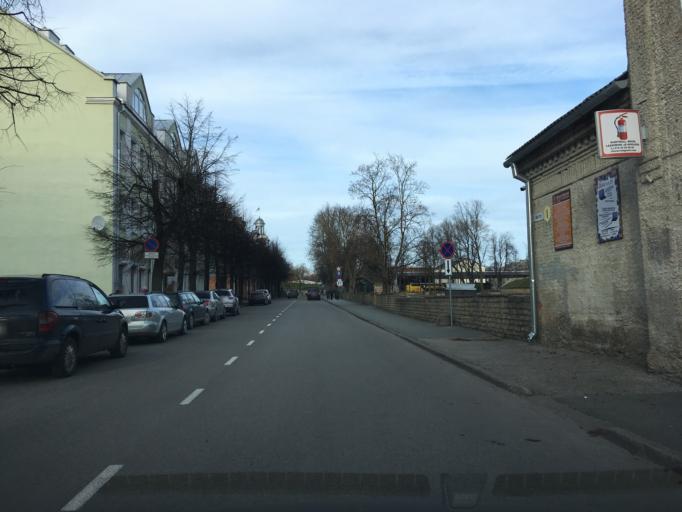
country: EE
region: Ida-Virumaa
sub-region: Narva linn
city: Narva
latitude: 59.3743
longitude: 28.1976
